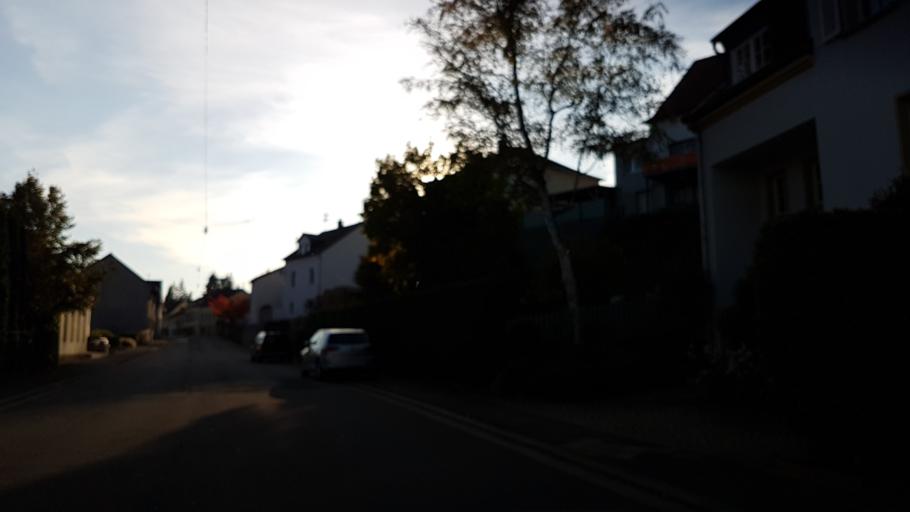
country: DE
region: Saarland
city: Lebach
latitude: 49.4153
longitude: 6.9152
